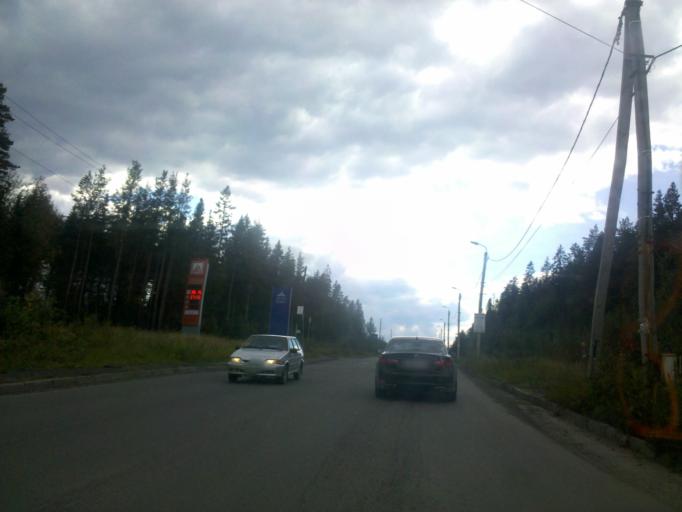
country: RU
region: Republic of Karelia
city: Petrozavodsk
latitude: 61.7783
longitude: 34.3064
